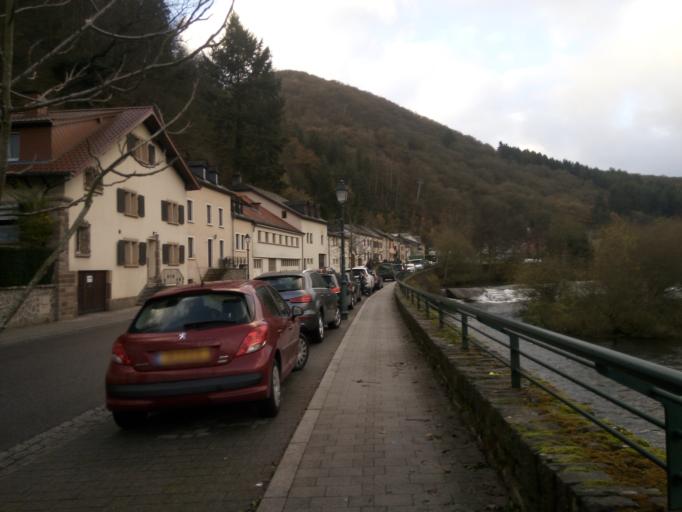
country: LU
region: Diekirch
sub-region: Canton de Vianden
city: Vianden
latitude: 49.9346
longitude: 6.2055
